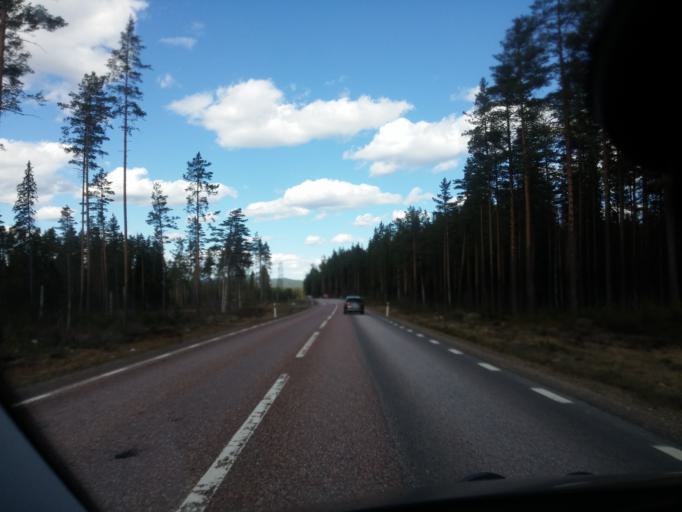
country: SE
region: Dalarna
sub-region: Faluns Kommun
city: Svardsjo
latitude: 60.7786
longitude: 15.7530
